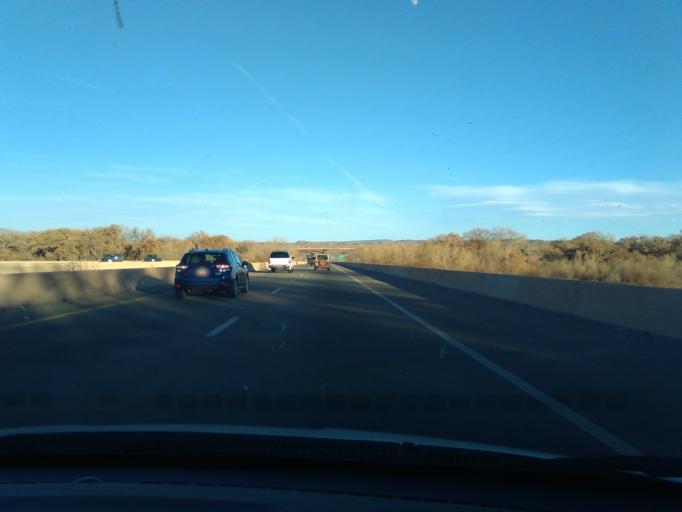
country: US
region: New Mexico
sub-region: Bernalillo County
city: South Valley
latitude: 34.9497
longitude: -106.6830
